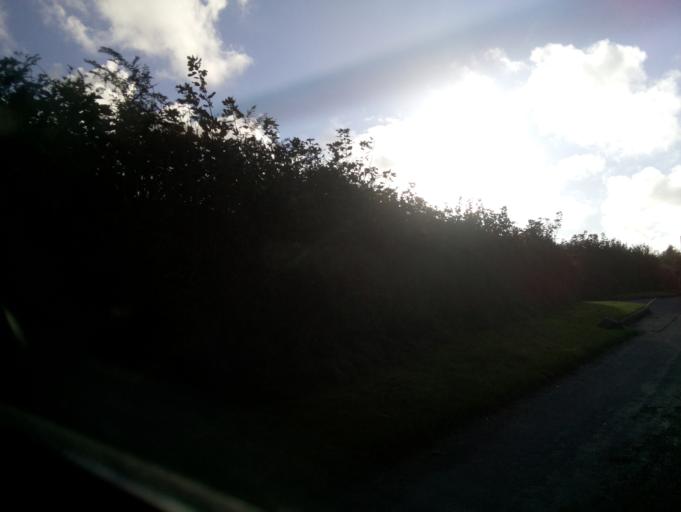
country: GB
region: England
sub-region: Devon
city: Totnes
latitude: 50.3459
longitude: -3.6758
